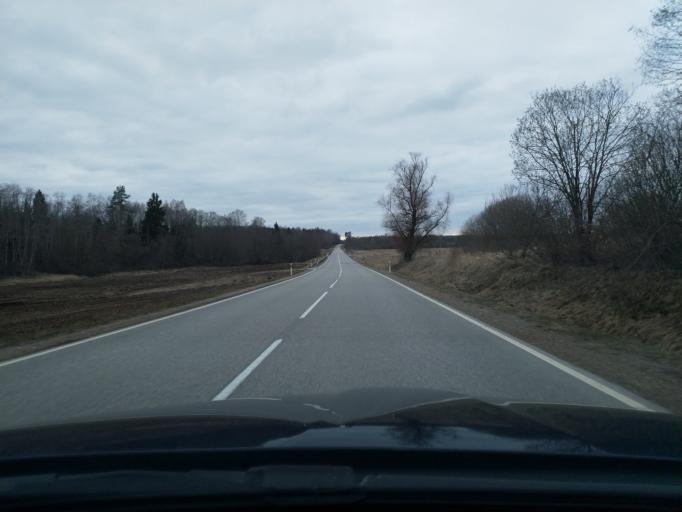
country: LV
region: Kuldigas Rajons
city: Kuldiga
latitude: 56.9657
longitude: 22.0618
